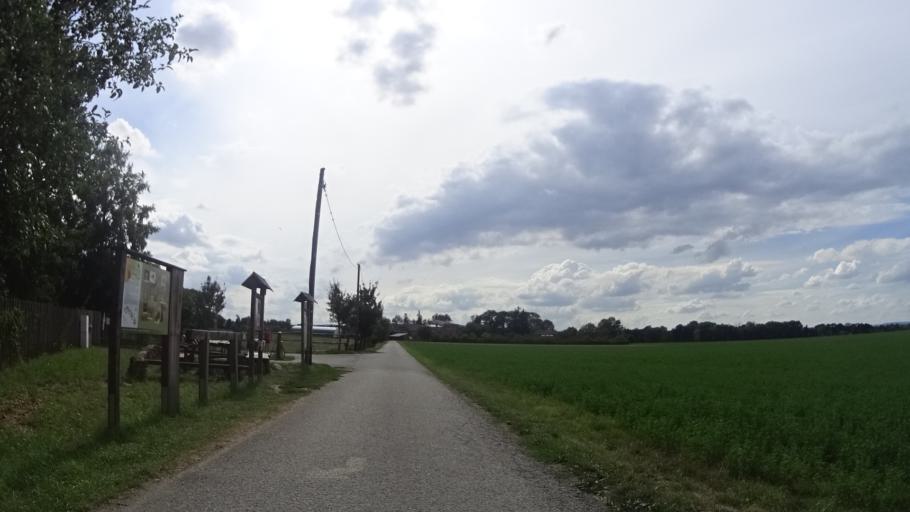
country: CZ
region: Olomoucky
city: Litovel
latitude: 49.6924
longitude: 17.1010
